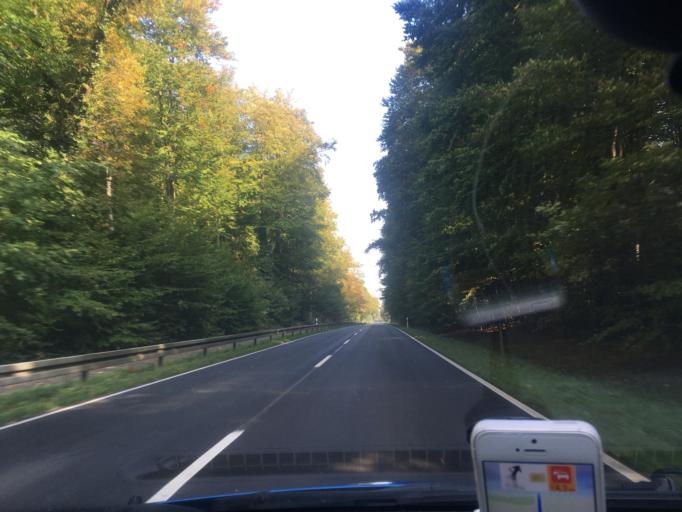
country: DE
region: Mecklenburg-Vorpommern
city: Hagenow
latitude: 53.4288
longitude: 11.1526
